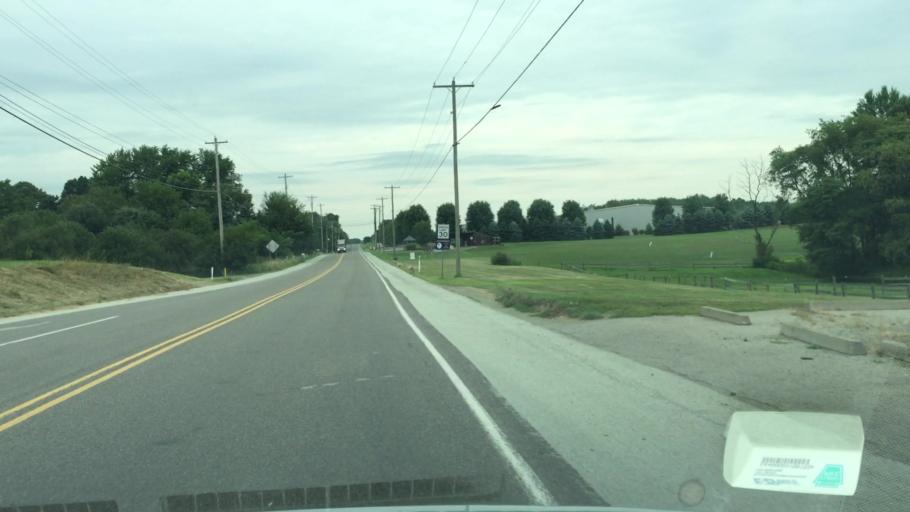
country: US
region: Pennsylvania
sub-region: Butler County
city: Saxonburg
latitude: 40.7226
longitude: -79.8527
